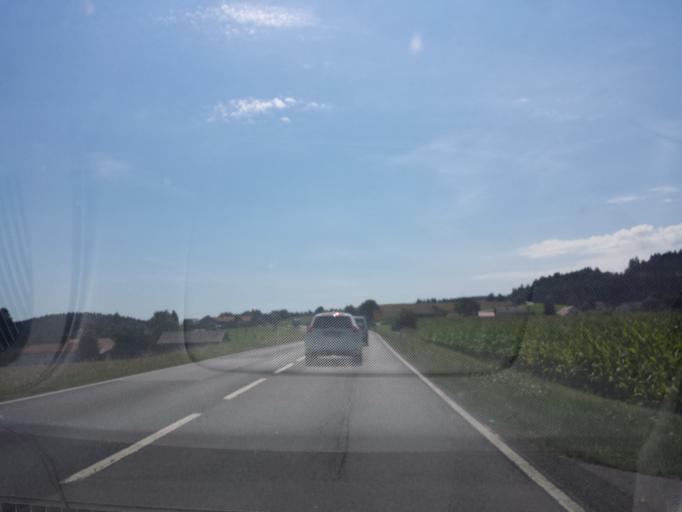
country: DE
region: Bavaria
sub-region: Upper Palatinate
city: Traitsching
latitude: 49.1215
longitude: 12.6503
